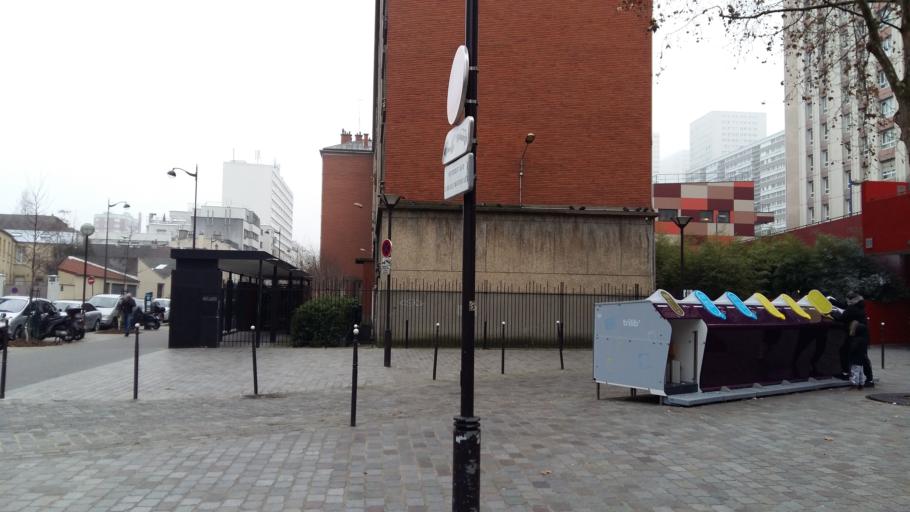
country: FR
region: Ile-de-France
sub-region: Departement du Val-de-Marne
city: Le Kremlin-Bicetre
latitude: 48.8257
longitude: 2.3670
